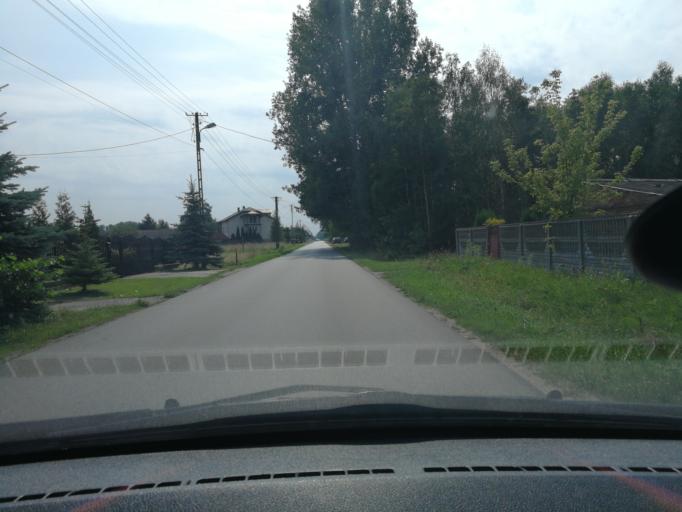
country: PL
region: Lodz Voivodeship
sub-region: Powiat skierniewicki
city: Makow
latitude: 52.0066
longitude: 20.0702
